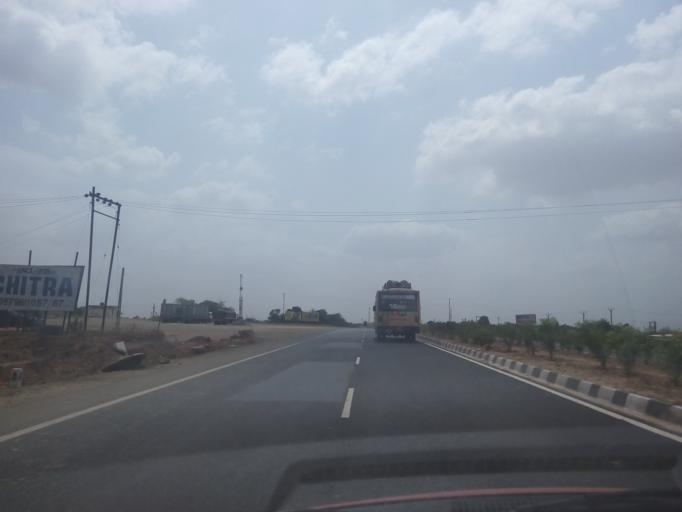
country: IN
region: Gujarat
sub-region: Surendranagar
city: Dhrangadhra
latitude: 23.0019
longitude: 71.3781
